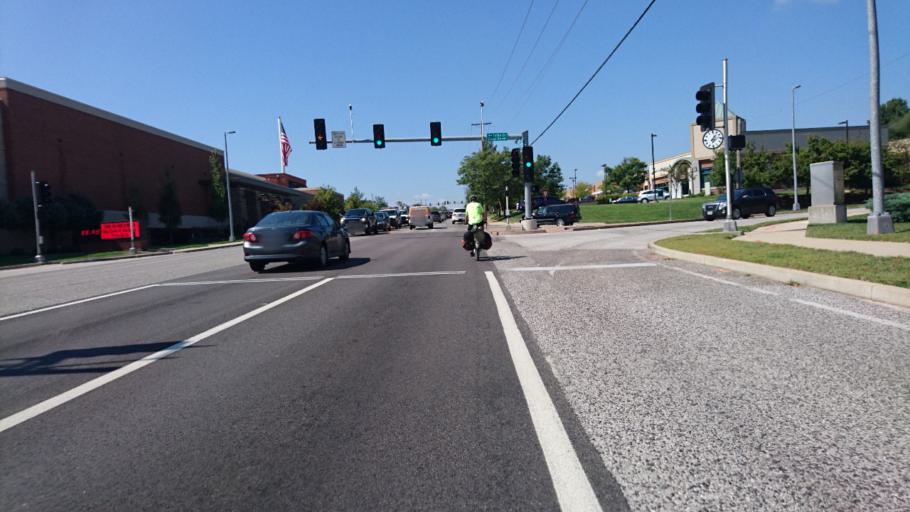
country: US
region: Missouri
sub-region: Saint Louis County
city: Des Peres
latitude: 38.6011
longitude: -90.4316
